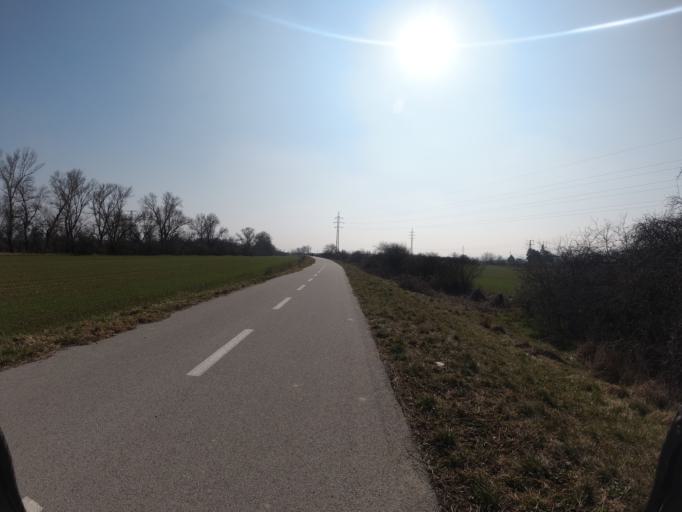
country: SK
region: Trenciansky
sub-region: Okres Nove Mesto nad Vahom
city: Nove Mesto nad Vahom
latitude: 48.7433
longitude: 17.8479
